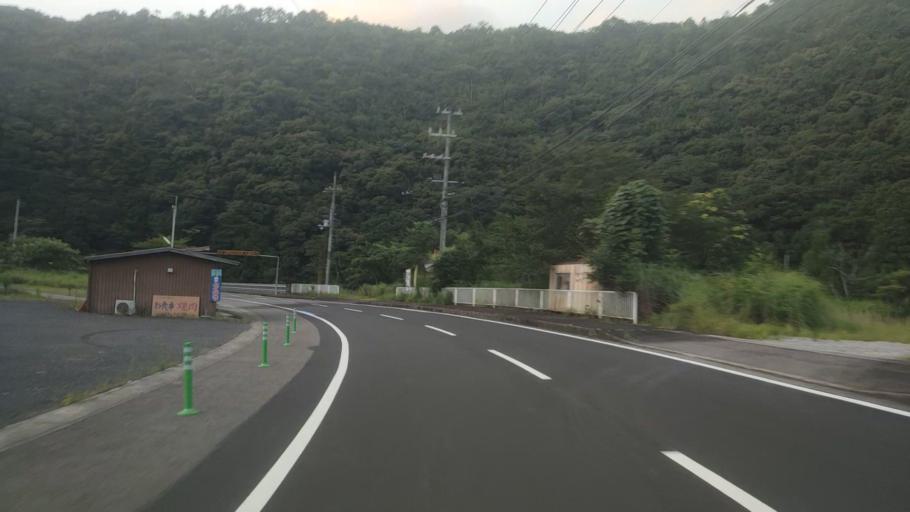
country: JP
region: Wakayama
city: Shingu
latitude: 33.8232
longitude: 135.7763
